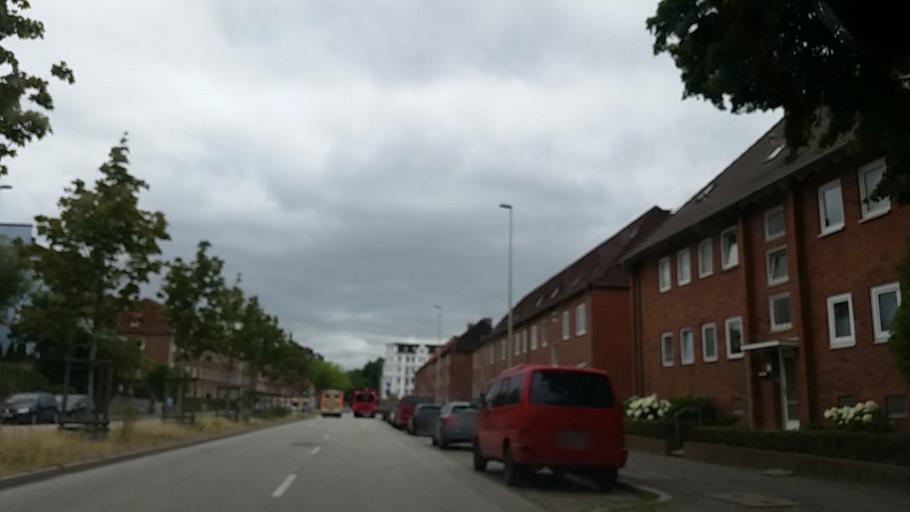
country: DE
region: Schleswig-Holstein
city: Kiel
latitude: 54.3259
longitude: 10.1107
